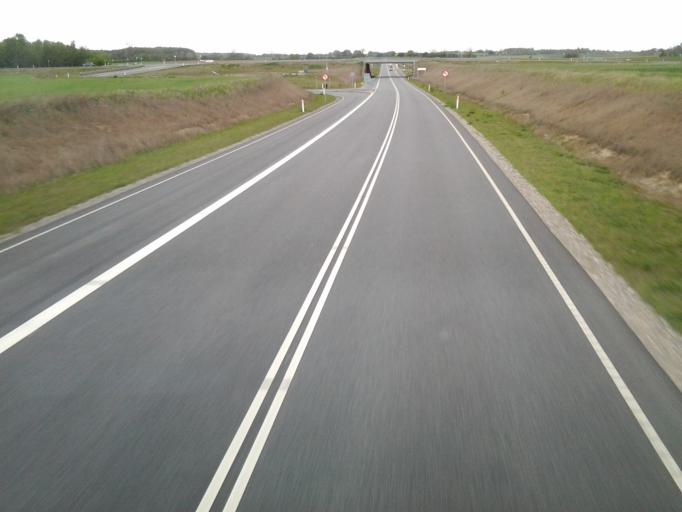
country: DK
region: Zealand
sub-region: Guldborgsund Kommune
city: Nykobing Falster
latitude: 54.7560
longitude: 11.9210
